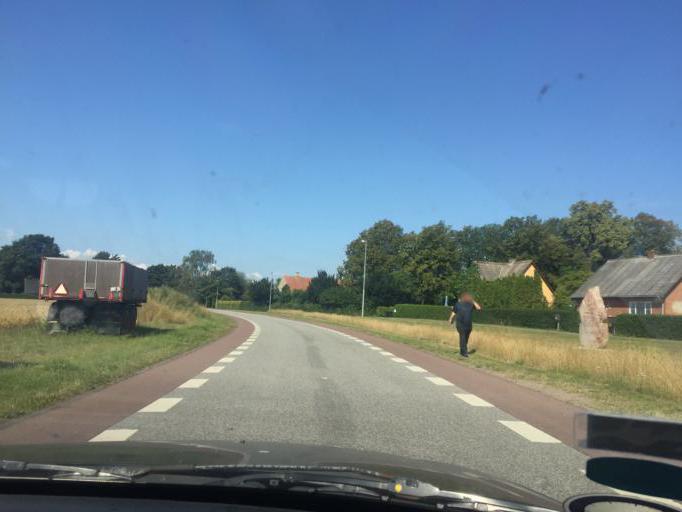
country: DK
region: Zealand
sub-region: Lolland Kommune
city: Maribo
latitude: 54.7982
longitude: 11.5209
